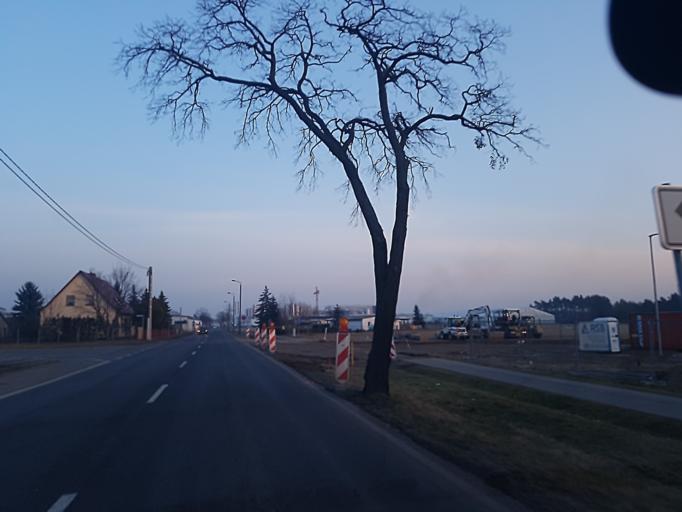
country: DE
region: Saxony-Anhalt
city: Jessen
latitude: 51.7968
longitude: 12.9438
